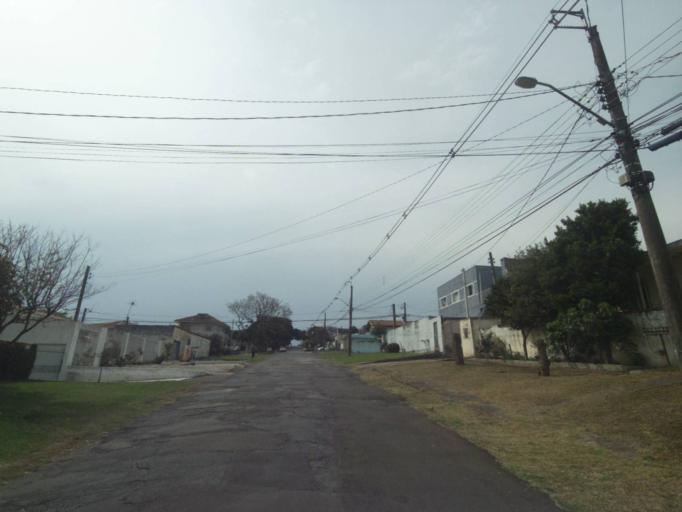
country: BR
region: Parana
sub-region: Pinhais
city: Pinhais
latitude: -25.4215
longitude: -49.2034
